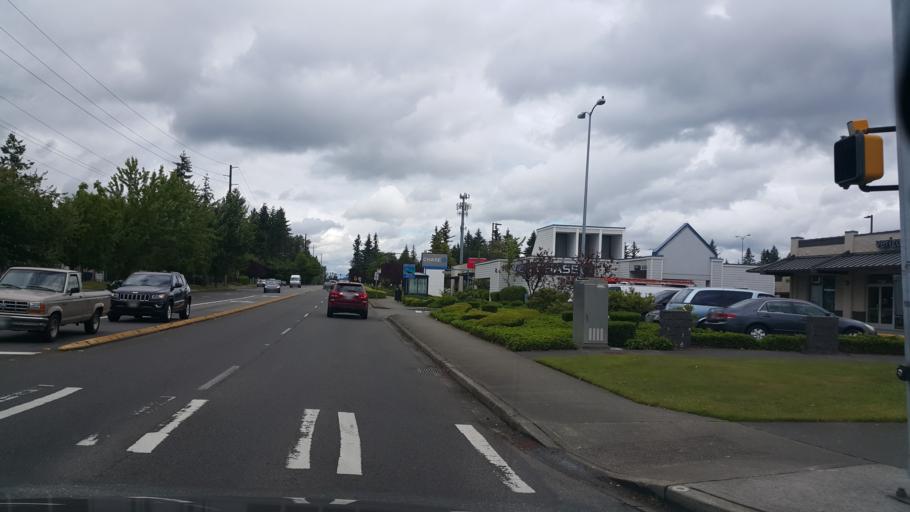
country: US
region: Washington
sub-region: King County
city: Fairwood
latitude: 47.4456
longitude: -122.1541
